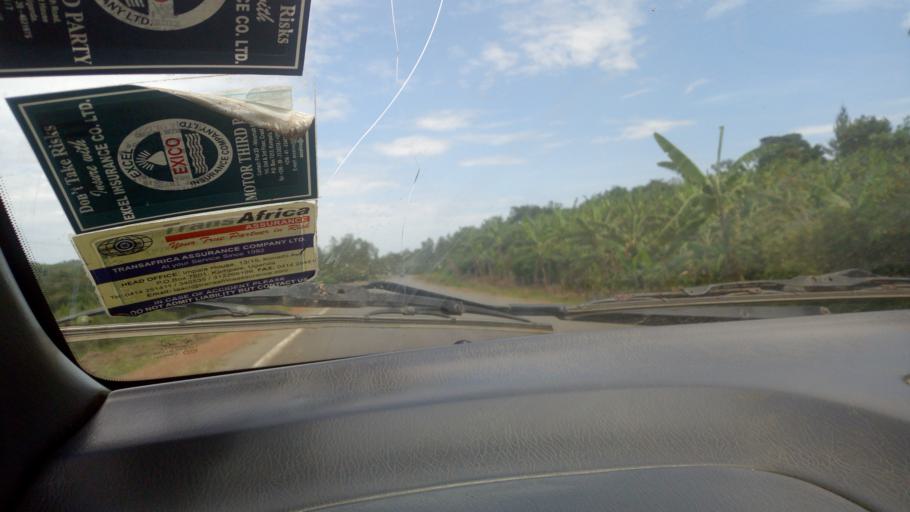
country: UG
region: Western Region
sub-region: Mbarara District
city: Bwizibwera
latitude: -0.3711
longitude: 30.5646
